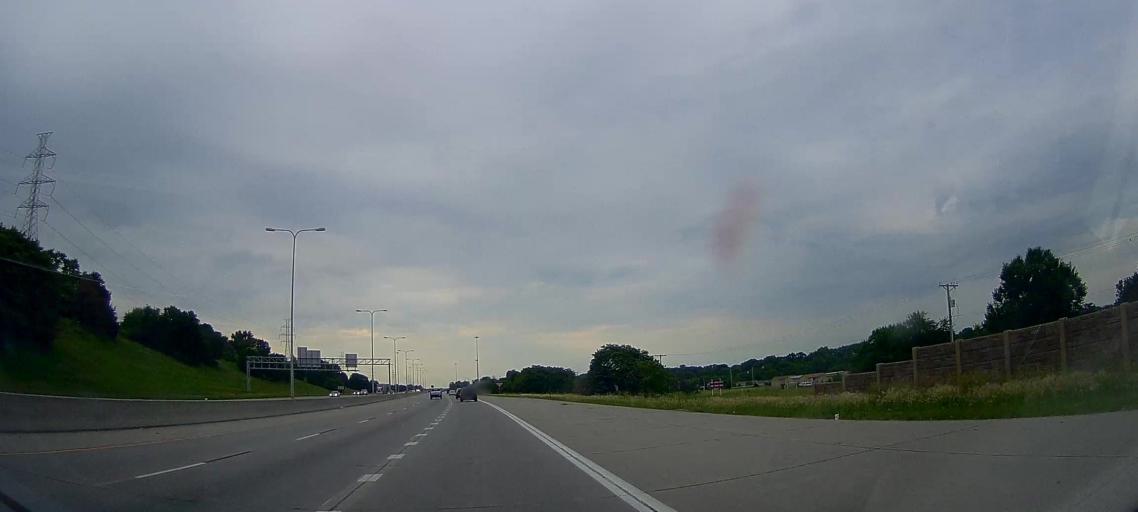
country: US
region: Nebraska
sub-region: Douglas County
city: Ralston
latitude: 41.2995
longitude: -96.0707
